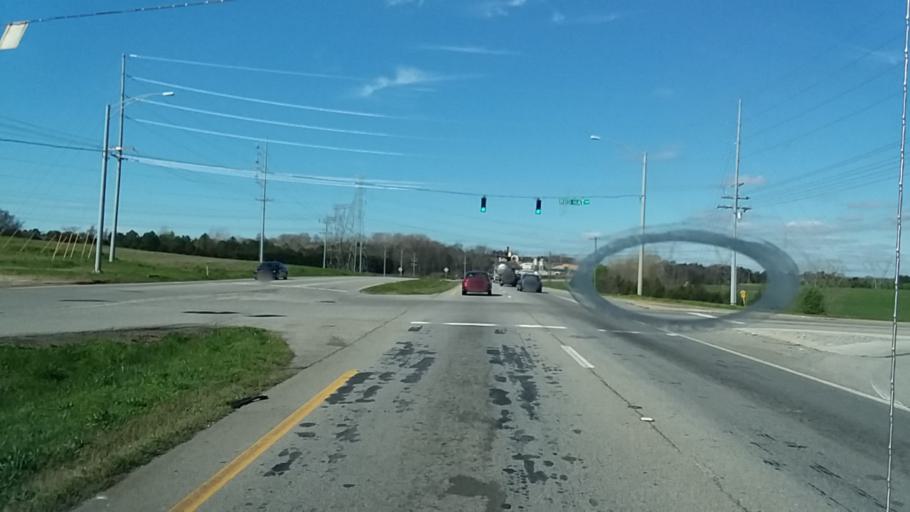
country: US
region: Alabama
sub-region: Morgan County
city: Trinity
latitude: 34.6201
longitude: -87.0698
